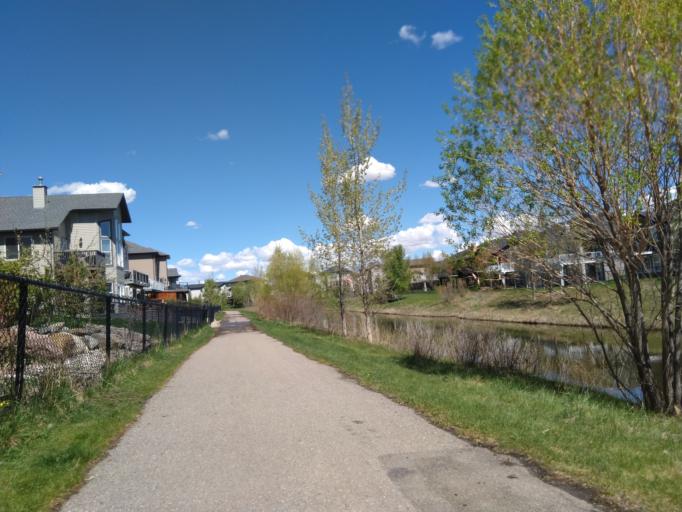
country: CA
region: Alberta
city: Chestermere
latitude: 51.0291
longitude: -113.8361
